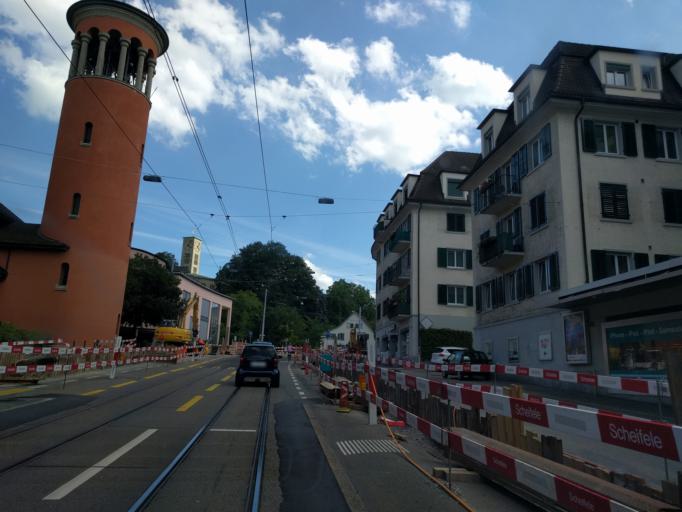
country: CH
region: Zurich
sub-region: Bezirk Zuerich
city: Zuerich (Kreis 2) / Wollishofen
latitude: 47.3433
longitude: 8.5304
